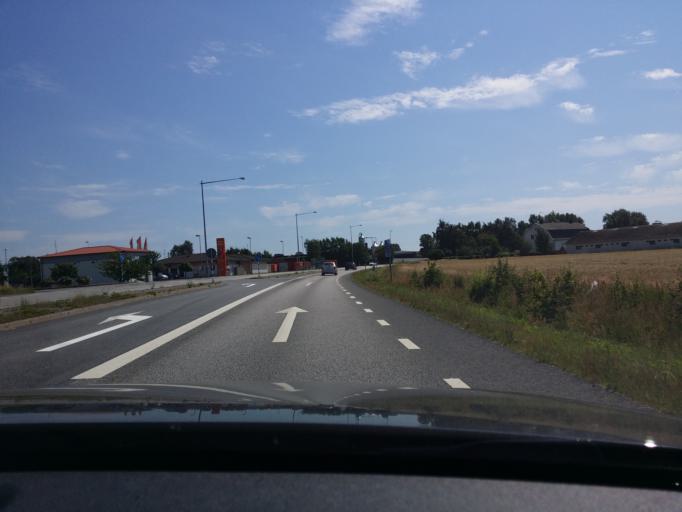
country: SE
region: Blekinge
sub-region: Solvesborgs Kommun
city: Soelvesborg
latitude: 56.0448
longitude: 14.6666
